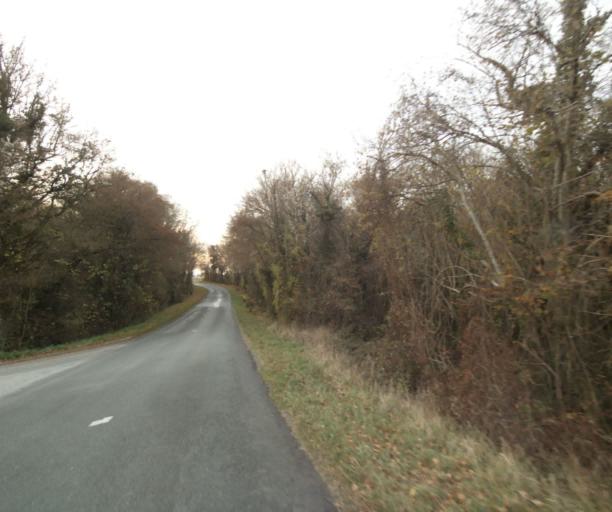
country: FR
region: Poitou-Charentes
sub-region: Departement de la Charente-Maritime
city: Bussac-sur-Charente
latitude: 45.8137
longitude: -0.6116
